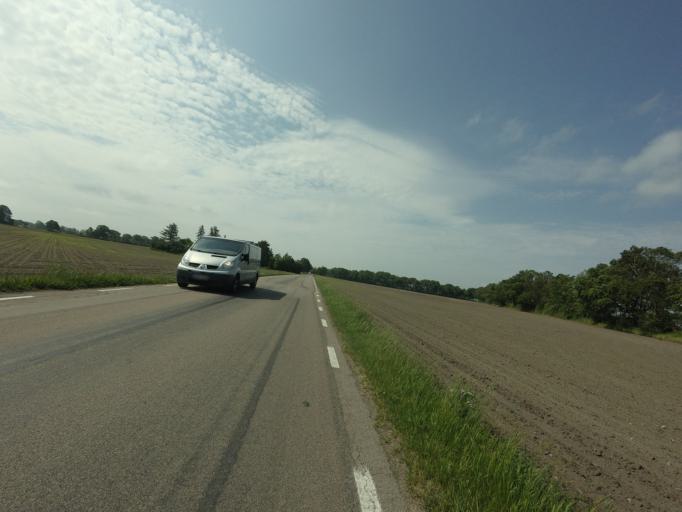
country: SE
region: Skane
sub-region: Helsingborg
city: Odakra
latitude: 56.2067
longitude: 12.7057
